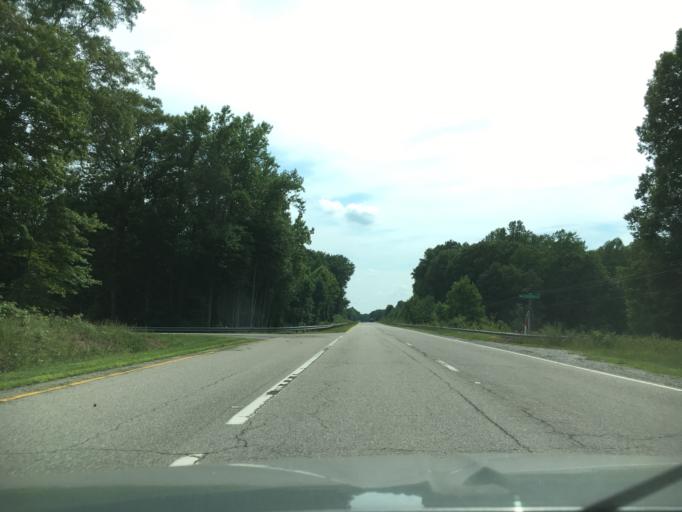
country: US
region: Virginia
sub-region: Lunenburg County
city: Victoria
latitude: 37.1458
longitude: -78.2960
